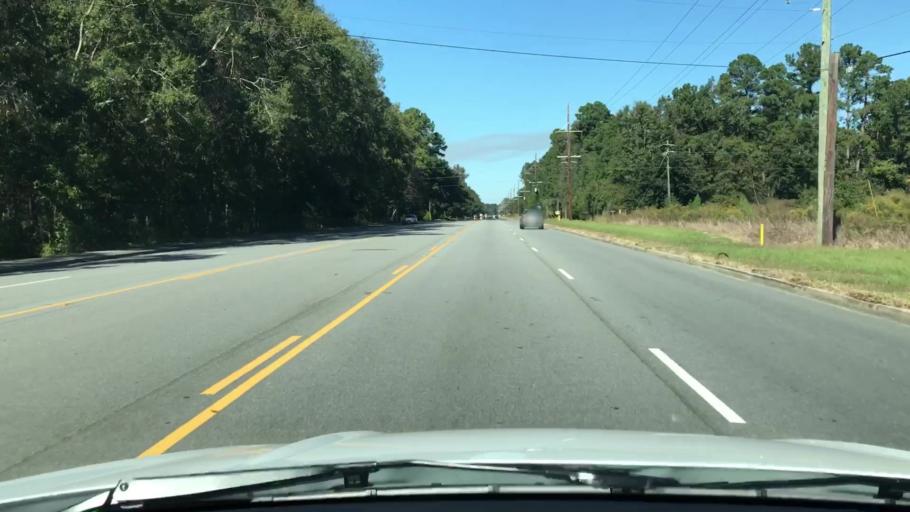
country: US
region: South Carolina
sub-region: Beaufort County
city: Laurel Bay
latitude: 32.5665
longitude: -80.7435
